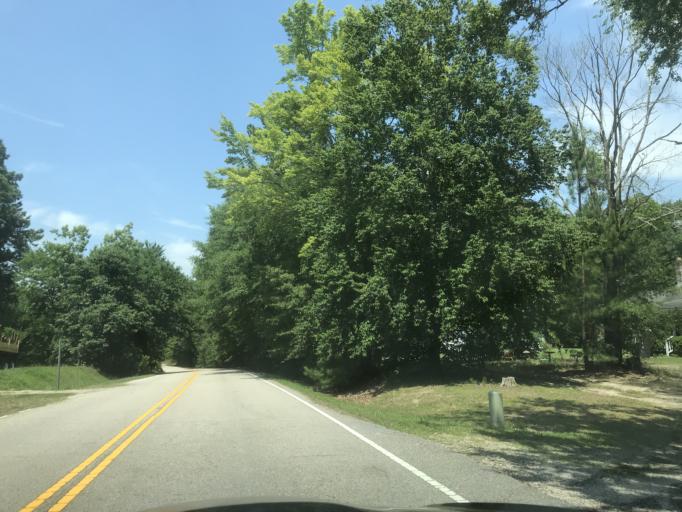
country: US
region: North Carolina
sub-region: Wake County
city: Wake Forest
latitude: 35.9342
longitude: -78.5793
